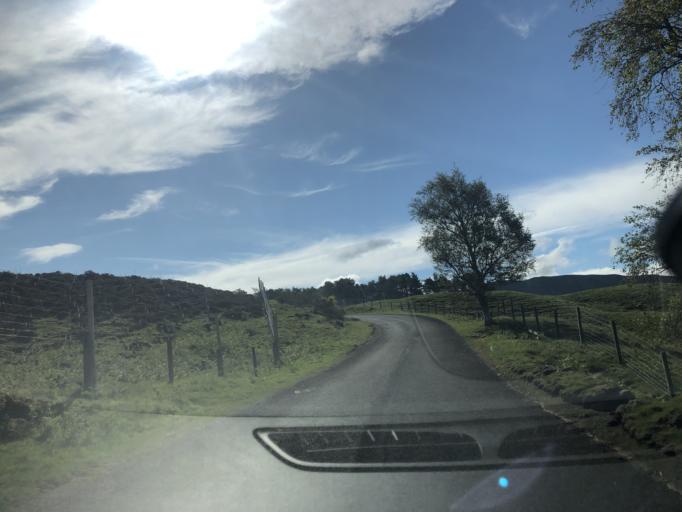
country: GB
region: Scotland
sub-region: Angus
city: Kirriemuir
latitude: 56.8272
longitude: -3.0529
